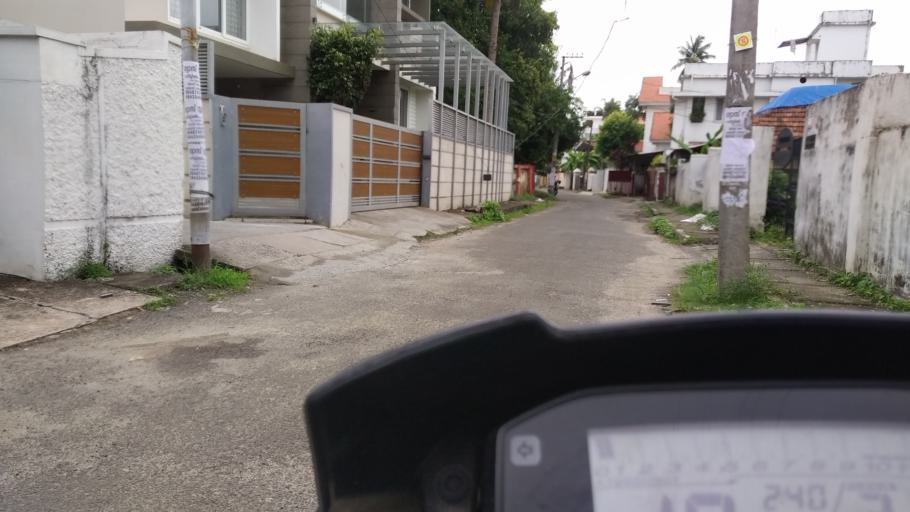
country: IN
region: Kerala
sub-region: Ernakulam
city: Cochin
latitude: 9.9985
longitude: 76.2814
